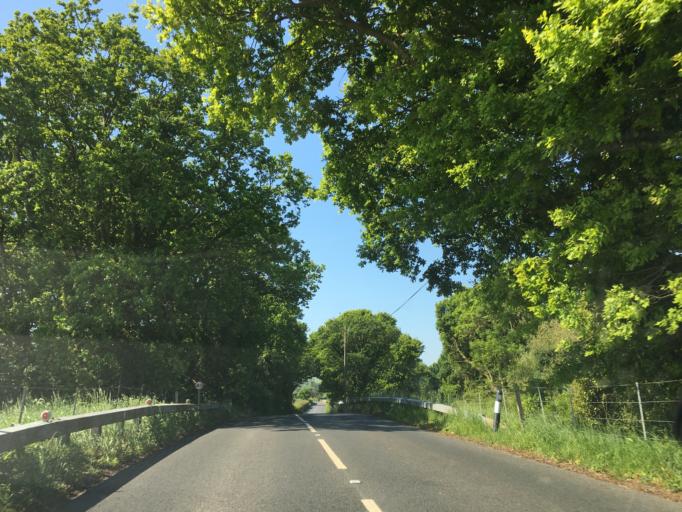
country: GB
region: England
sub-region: Isle of Wight
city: Ryde
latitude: 50.7019
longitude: -1.1683
